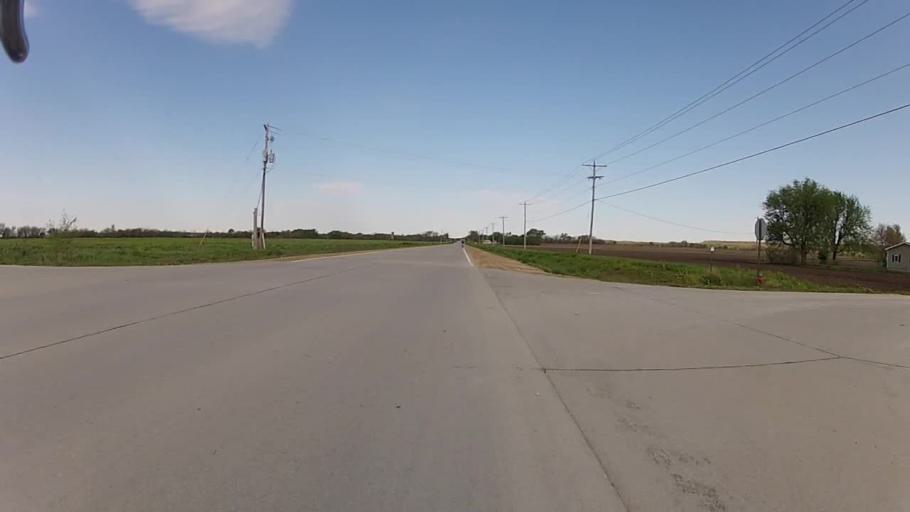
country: US
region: Kansas
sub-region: Riley County
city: Ogden
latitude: 39.1532
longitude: -96.6632
